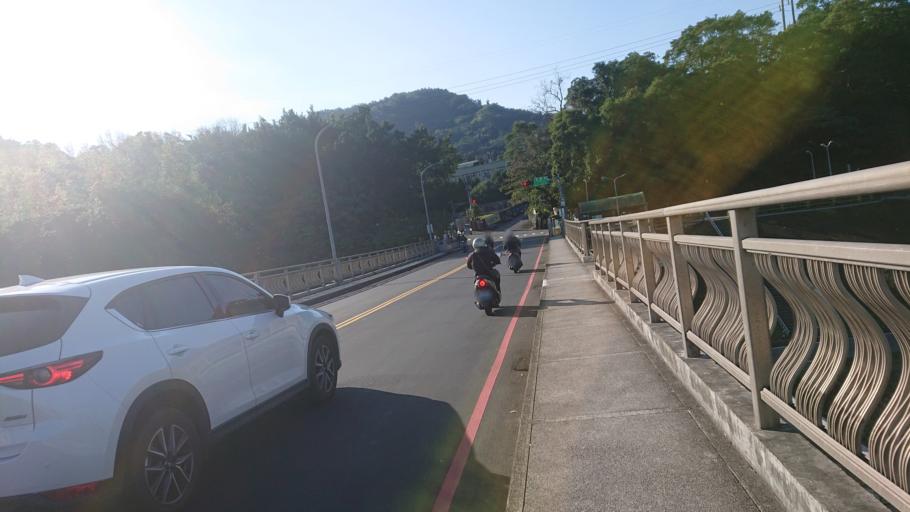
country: TW
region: Taipei
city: Taipei
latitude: 24.9805
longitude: 121.5675
